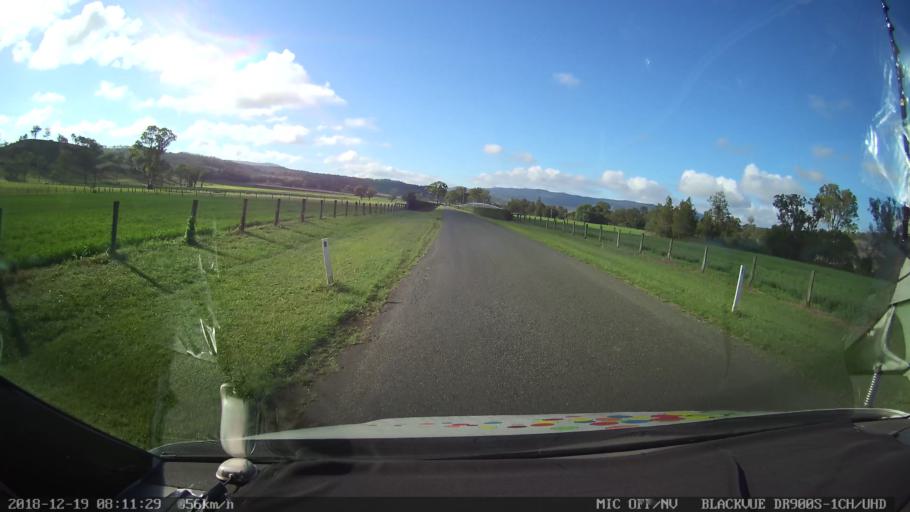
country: AU
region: Queensland
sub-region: Logan
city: Cedar Vale
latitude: -28.2189
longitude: 152.8913
